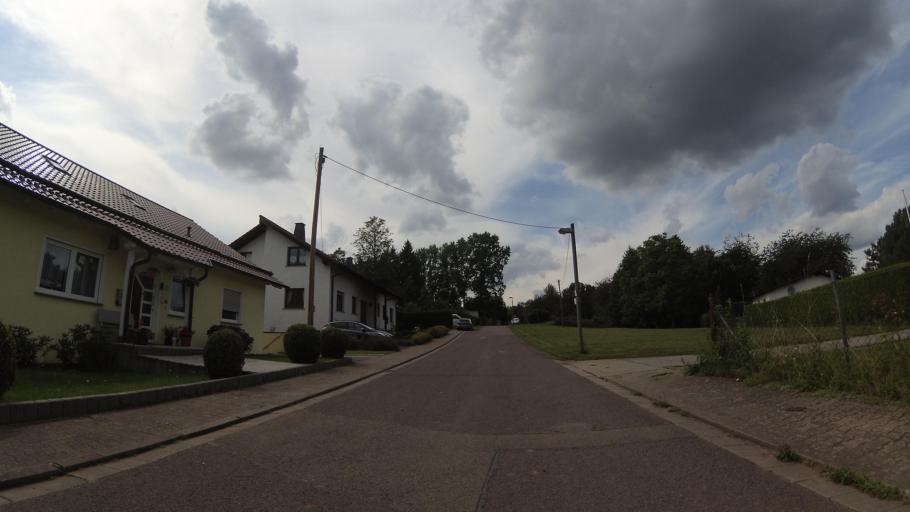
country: DE
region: Saarland
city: Illingen
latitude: 49.3760
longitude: 7.0711
